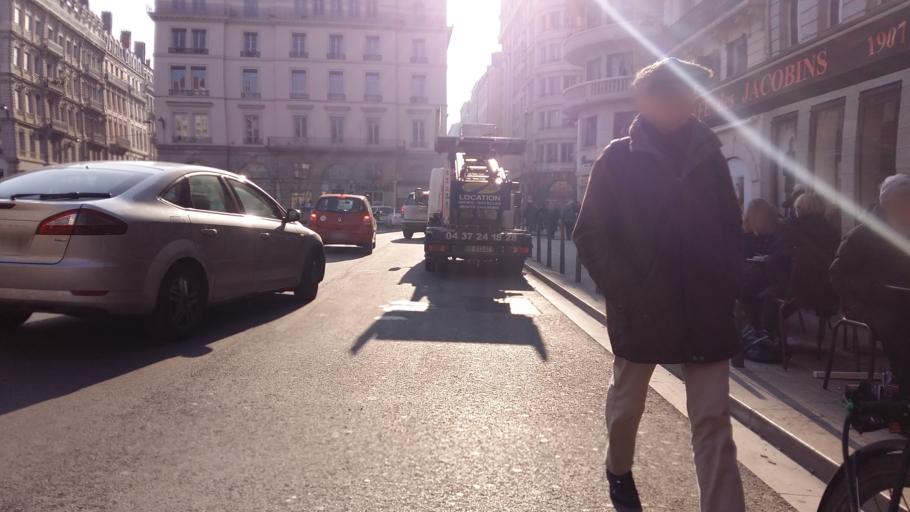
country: FR
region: Rhone-Alpes
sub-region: Departement du Rhone
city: Lyon
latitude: 45.7608
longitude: 4.8333
